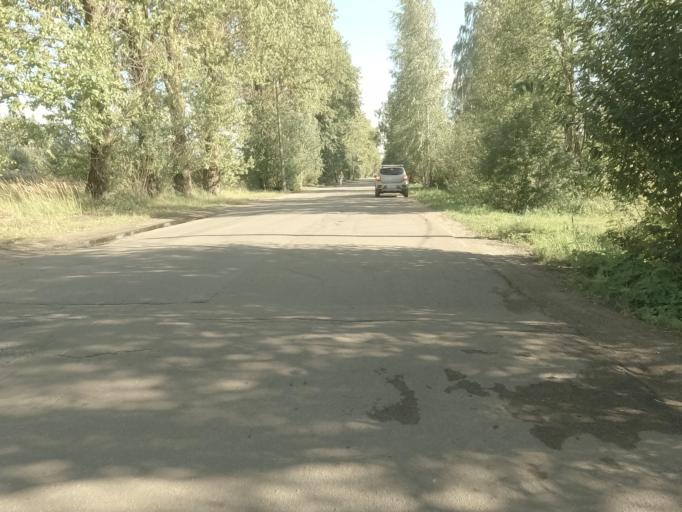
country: RU
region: Leningrad
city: Imeni Morozova
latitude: 59.9707
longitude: 31.0274
